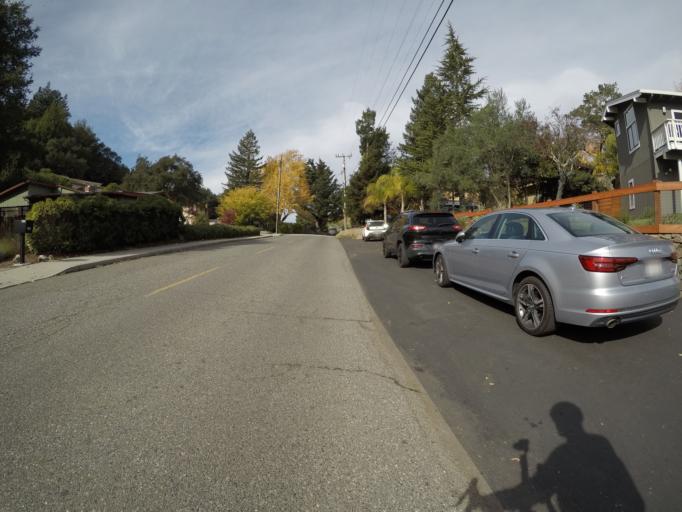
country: US
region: California
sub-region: Santa Cruz County
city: Scotts Valley
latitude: 37.0566
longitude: -121.9979
